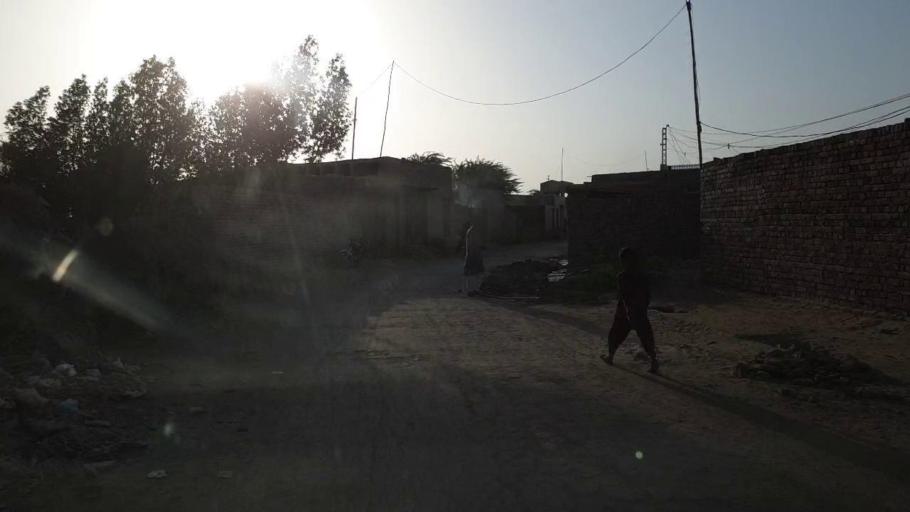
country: PK
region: Sindh
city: Jam Sahib
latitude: 26.2934
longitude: 68.6280
